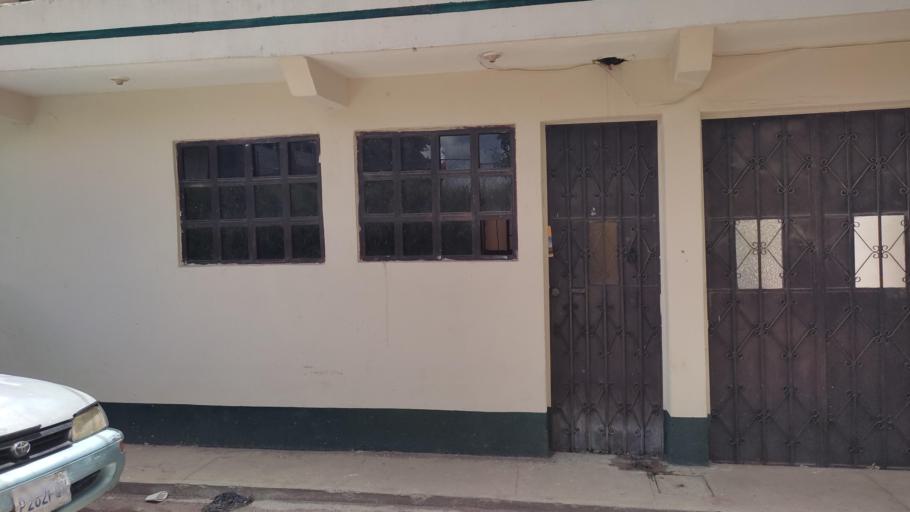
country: GT
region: Quetzaltenango
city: Olintepeque
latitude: 14.8625
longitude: -91.5332
